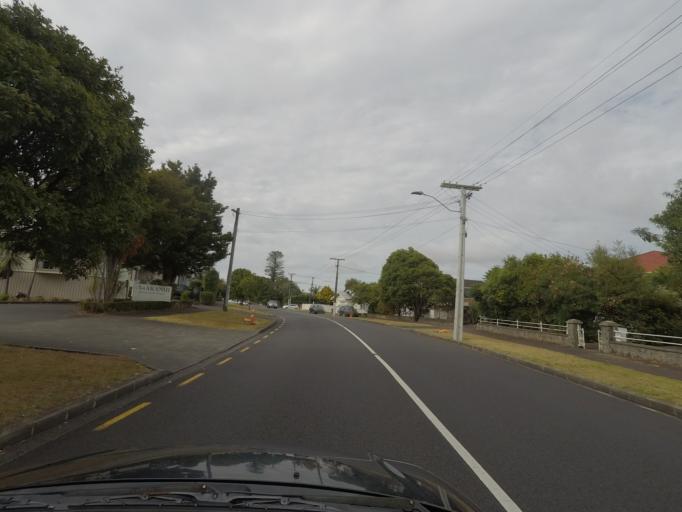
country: NZ
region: Auckland
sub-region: Auckland
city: Rosebank
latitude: -36.8859
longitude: 174.7099
